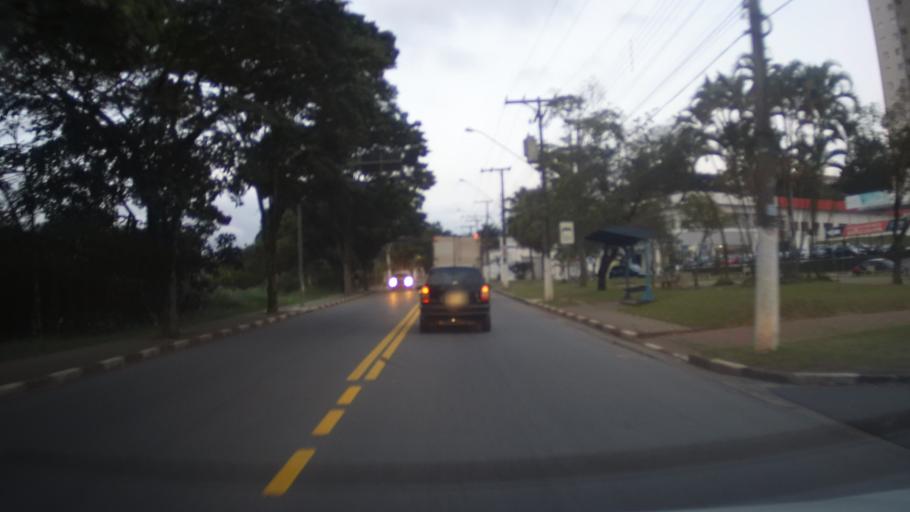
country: BR
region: Sao Paulo
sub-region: Aruja
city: Aruja
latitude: -23.3897
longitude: -46.3158
